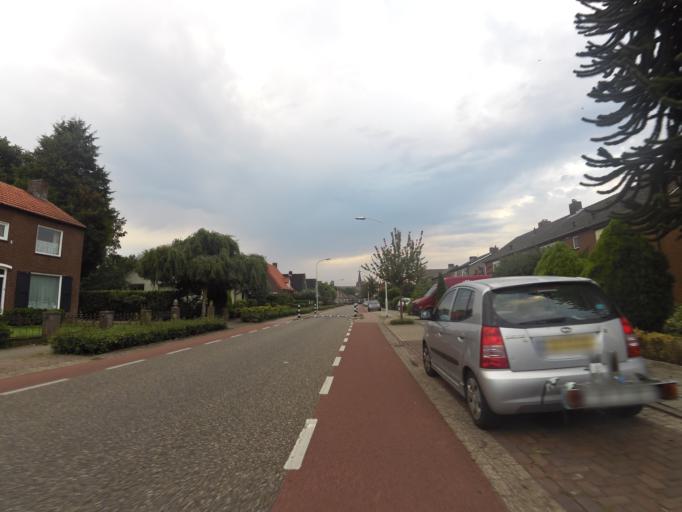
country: NL
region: Gelderland
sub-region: Oude IJsselstreek
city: Gendringen
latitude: 51.9144
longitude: 6.3444
